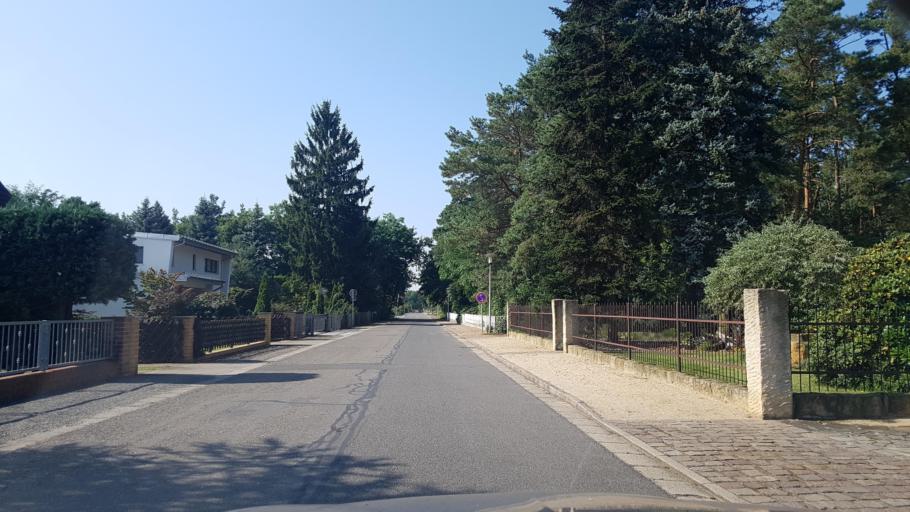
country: DE
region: Brandenburg
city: Bad Liebenwerda
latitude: 51.5027
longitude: 13.4326
